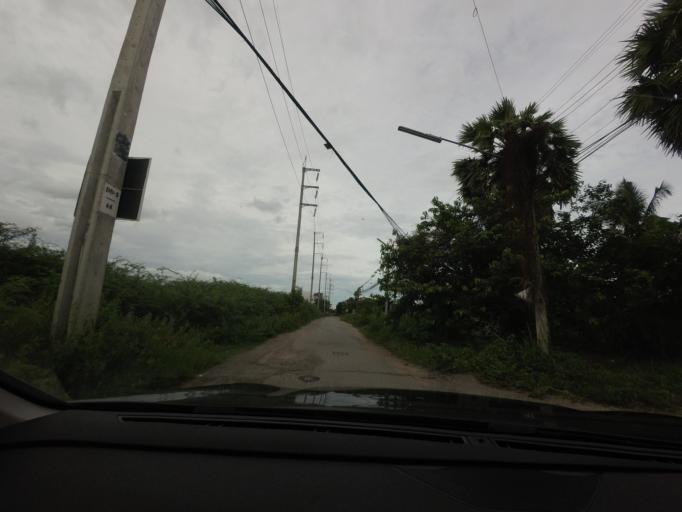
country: TH
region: Prachuap Khiri Khan
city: Hua Hin
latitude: 12.5372
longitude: 99.9468
